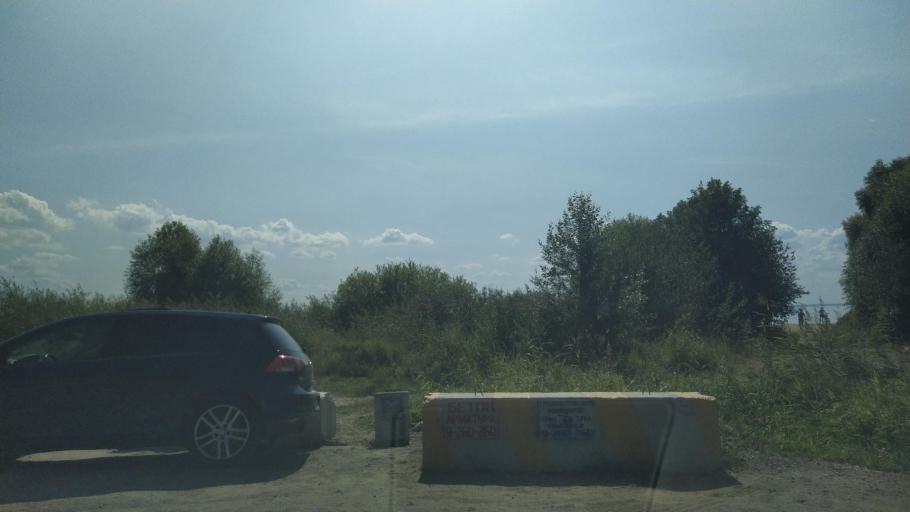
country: RU
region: St.-Petersburg
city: Lakhtinskiy
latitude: 59.9885
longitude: 30.1568
